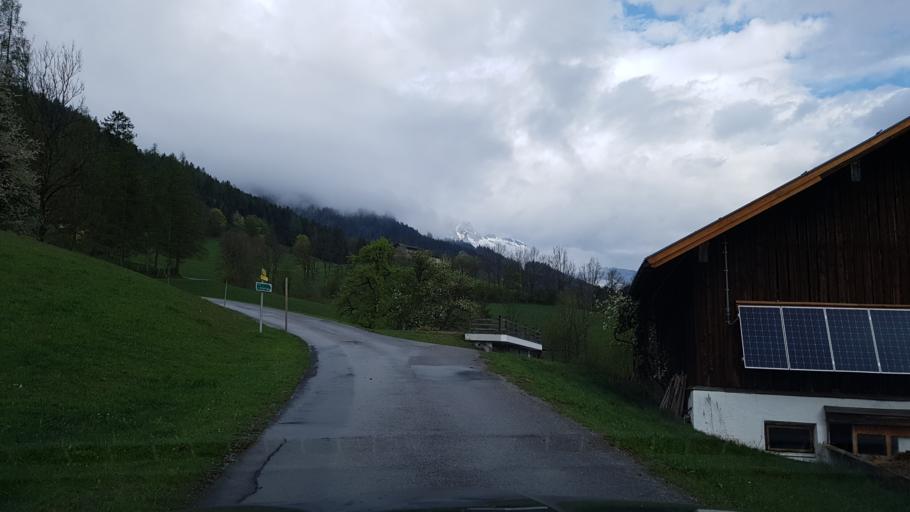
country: AT
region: Salzburg
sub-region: Politischer Bezirk Sankt Johann im Pongau
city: Werfen
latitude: 47.4639
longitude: 13.1873
